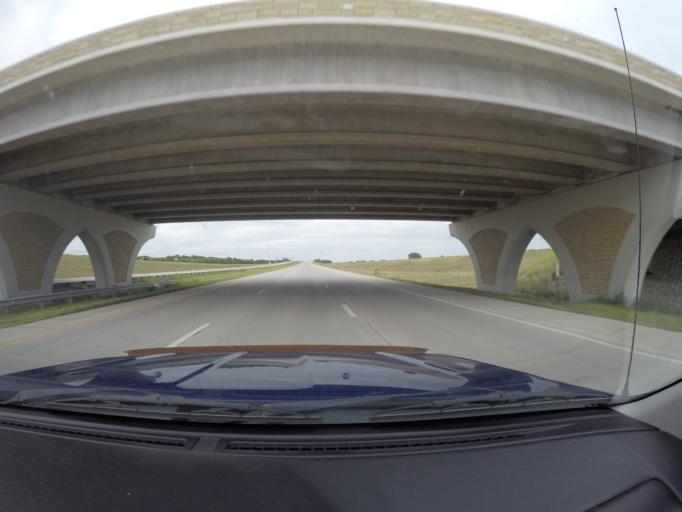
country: US
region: Kansas
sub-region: Riley County
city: Ogden
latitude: 39.1142
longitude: -96.6961
